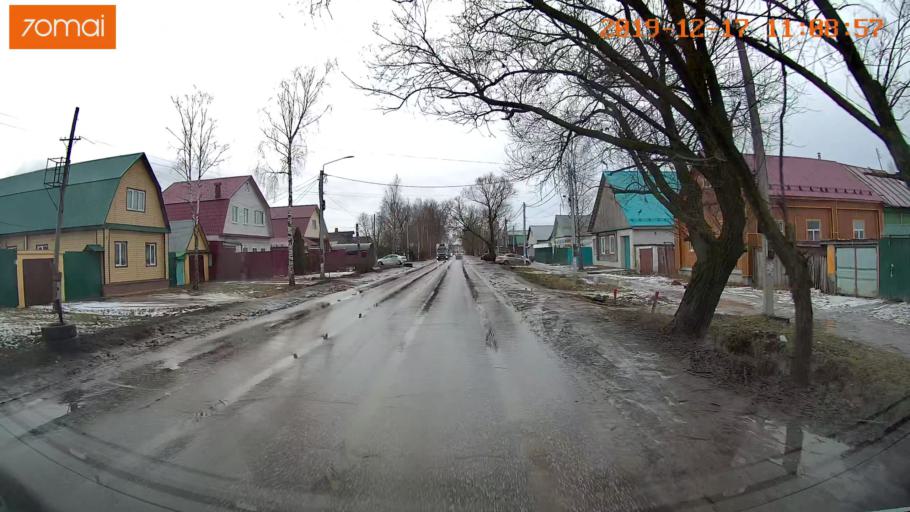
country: RU
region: Vladimir
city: Gus'-Khrustal'nyy
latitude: 55.6043
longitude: 40.6429
